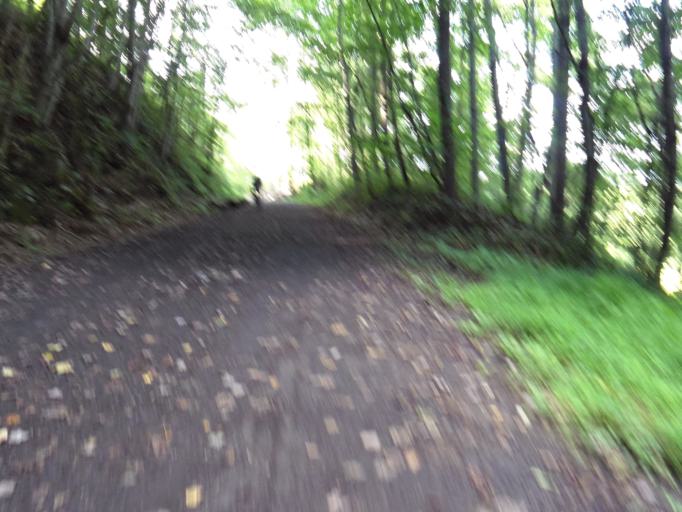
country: US
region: Virginia
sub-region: Washington County
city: Abingdon
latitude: 36.6963
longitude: -81.9423
